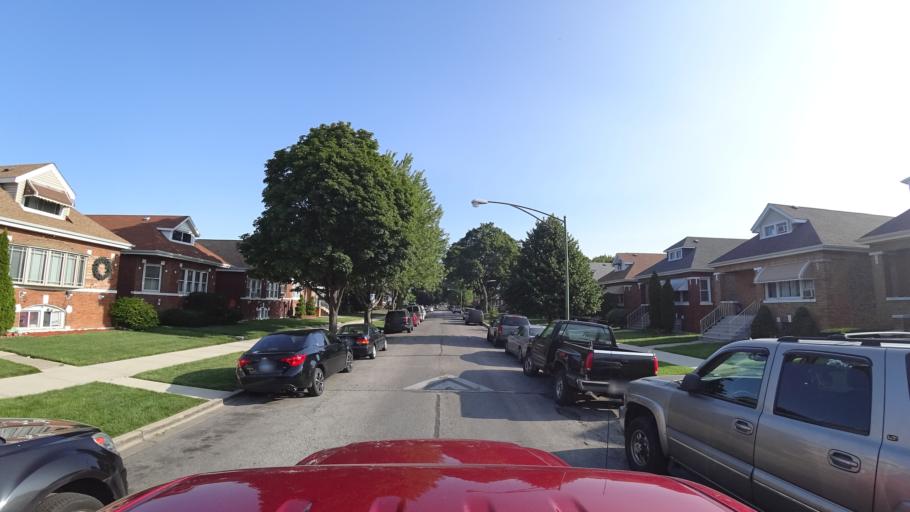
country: US
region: Illinois
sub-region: Cook County
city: Hometown
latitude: 41.7909
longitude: -87.7097
